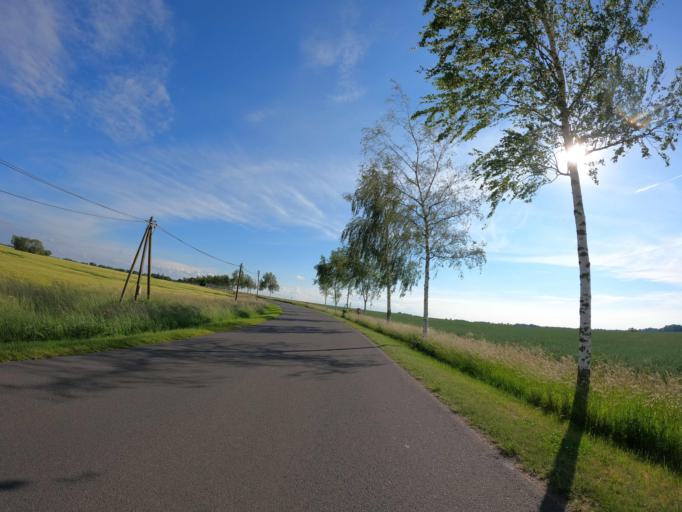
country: DE
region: Mecklenburg-Vorpommern
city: Preetz
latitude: 54.3432
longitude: 12.9743
